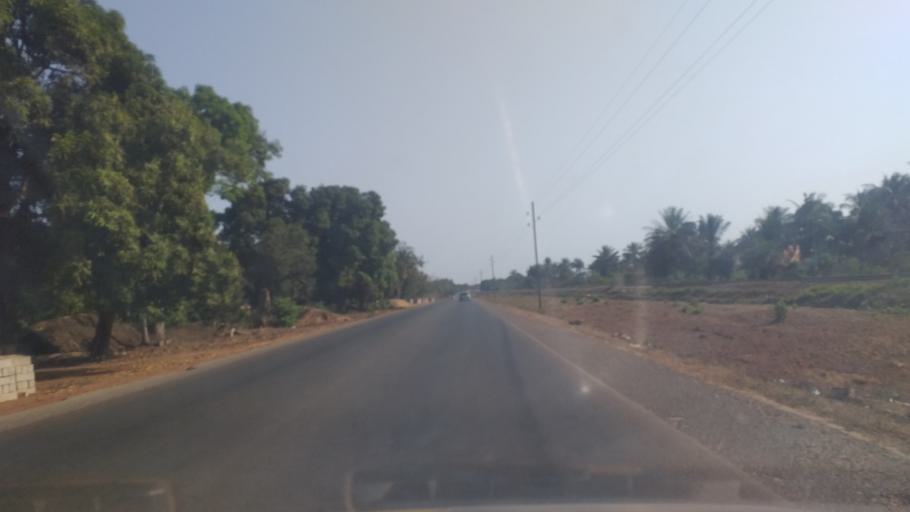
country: GN
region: Boke
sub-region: Boke Prefecture
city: Kamsar
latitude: 10.7253
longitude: -14.5191
